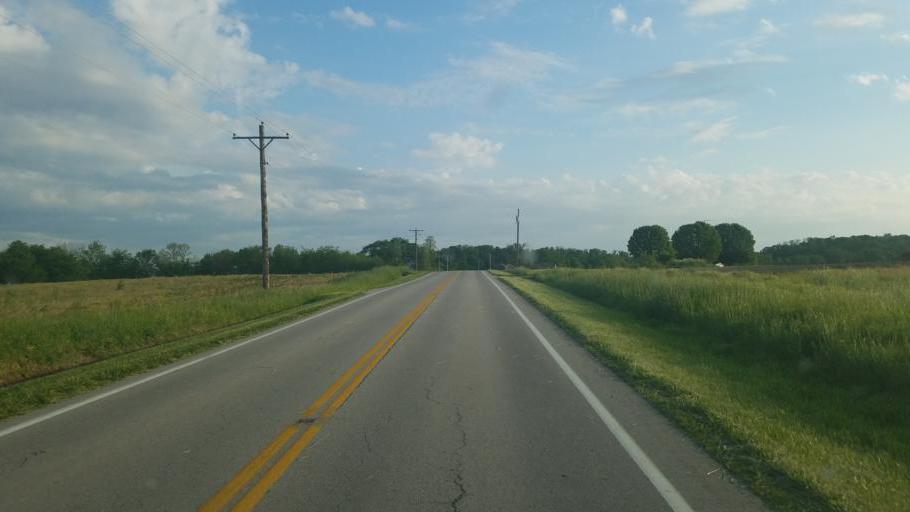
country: US
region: Ohio
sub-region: Highland County
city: Leesburg
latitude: 39.3860
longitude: -83.5946
